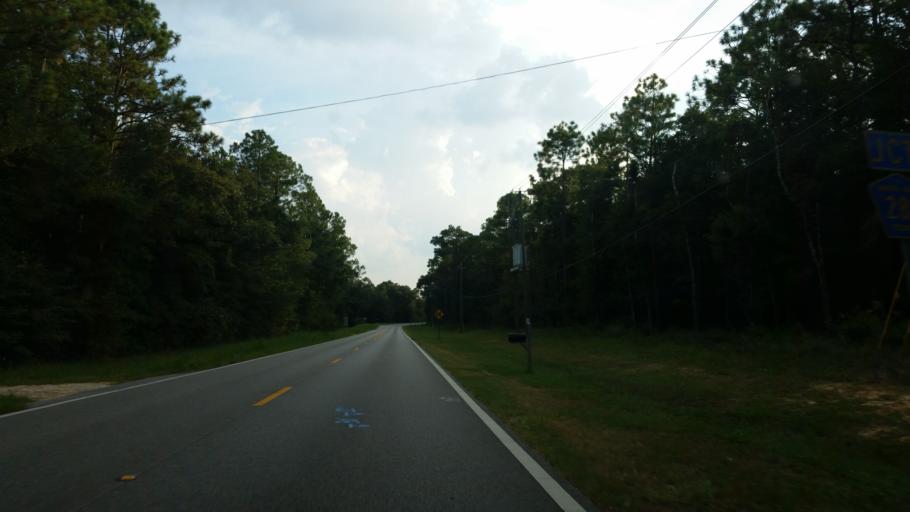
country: US
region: Florida
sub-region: Santa Rosa County
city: Pace
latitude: 30.5632
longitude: -87.1069
